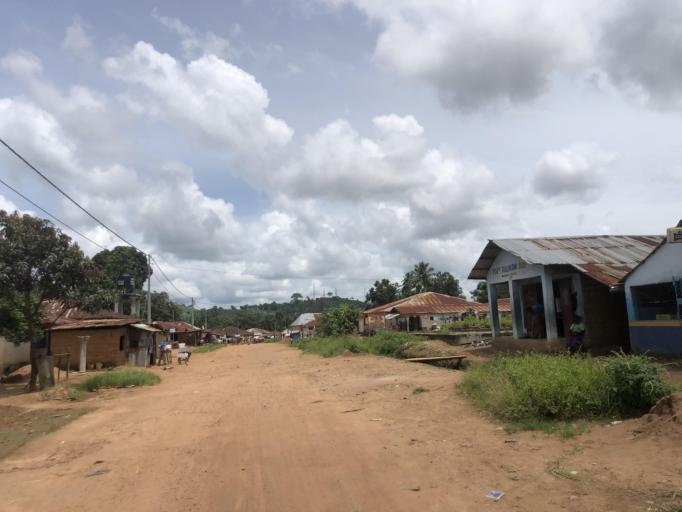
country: SL
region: Northern Province
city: Makeni
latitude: 8.8618
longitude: -12.0557
